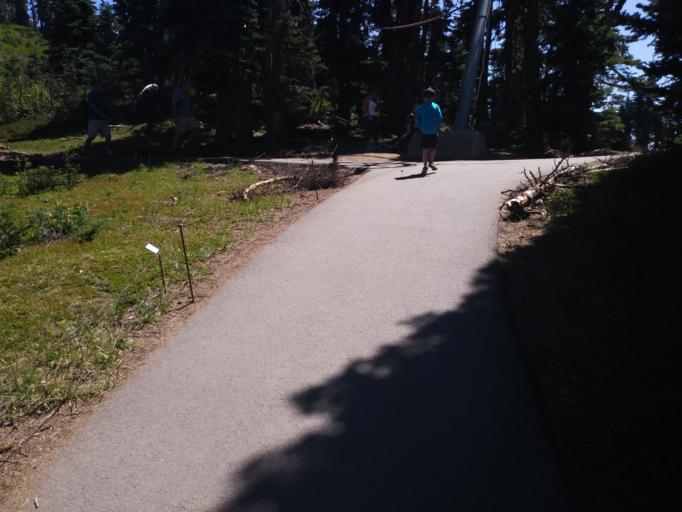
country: US
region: Washington
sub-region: Clallam County
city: Port Angeles
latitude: 47.9711
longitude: -123.4938
